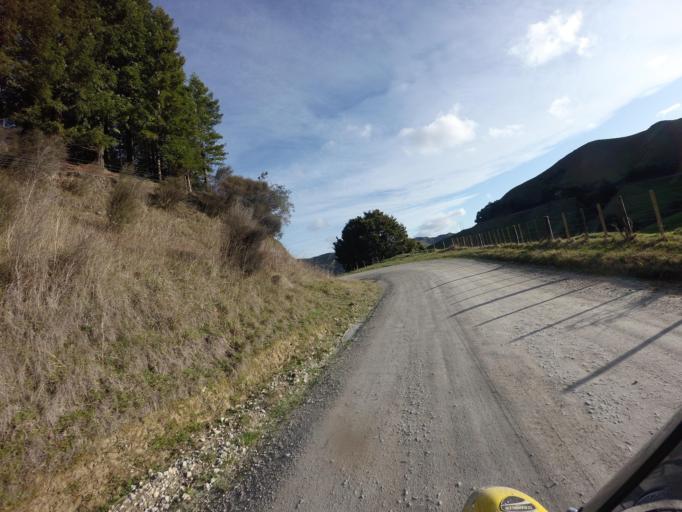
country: NZ
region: Hawke's Bay
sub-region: Wairoa District
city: Wairoa
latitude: -38.7200
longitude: 177.5798
